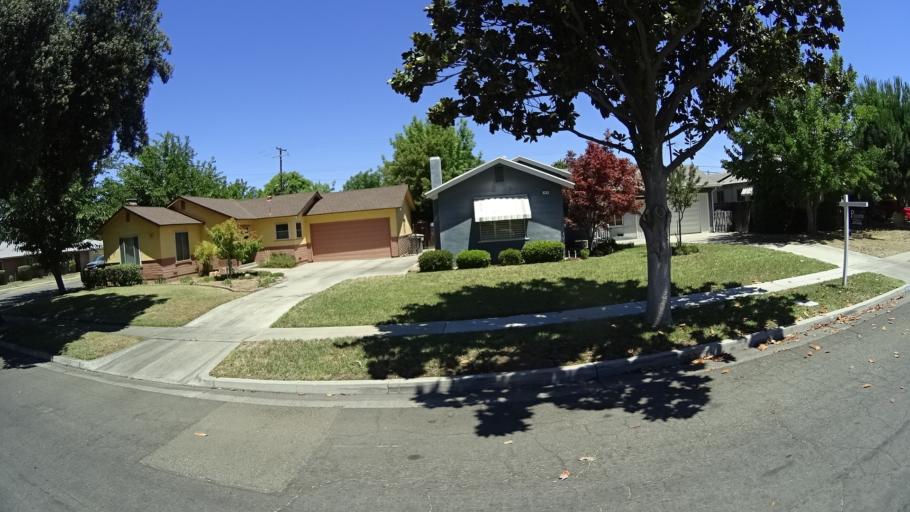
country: US
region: California
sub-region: Fresno County
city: Fresno
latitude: 36.7739
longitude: -119.8241
